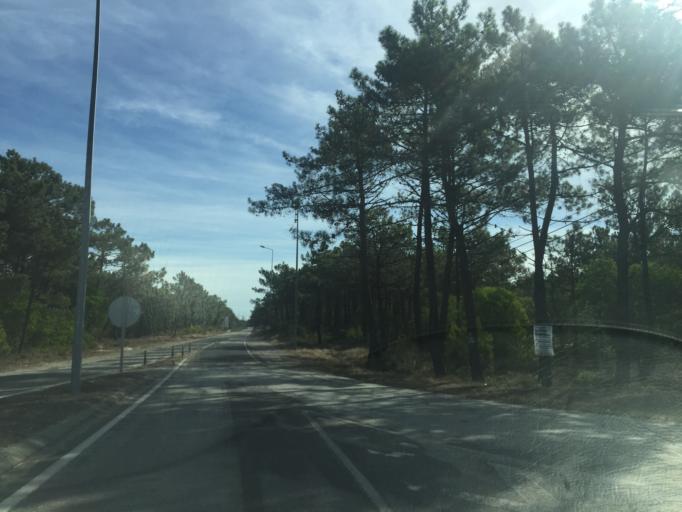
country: PT
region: Coimbra
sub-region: Figueira da Foz
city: Lavos
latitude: 40.0905
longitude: -8.8540
